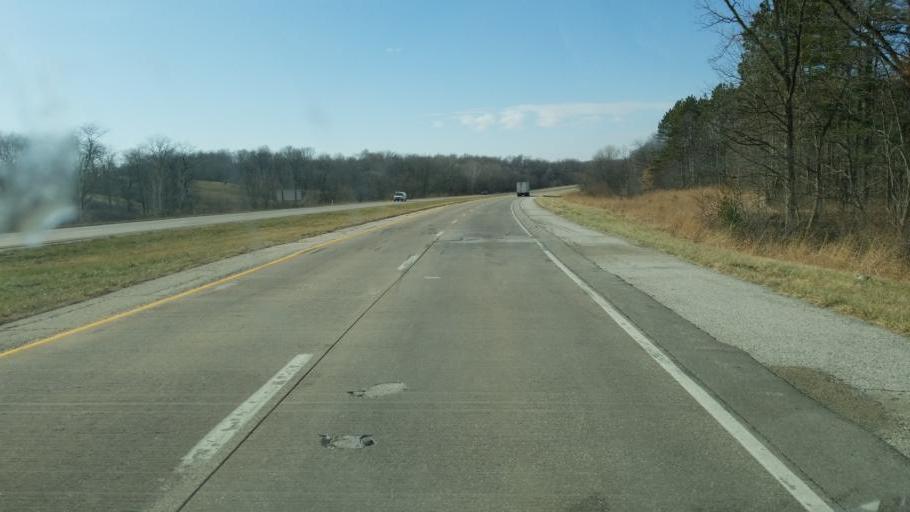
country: US
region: Illinois
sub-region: Warren County
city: Monmouth
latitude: 40.9214
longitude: -90.5413
